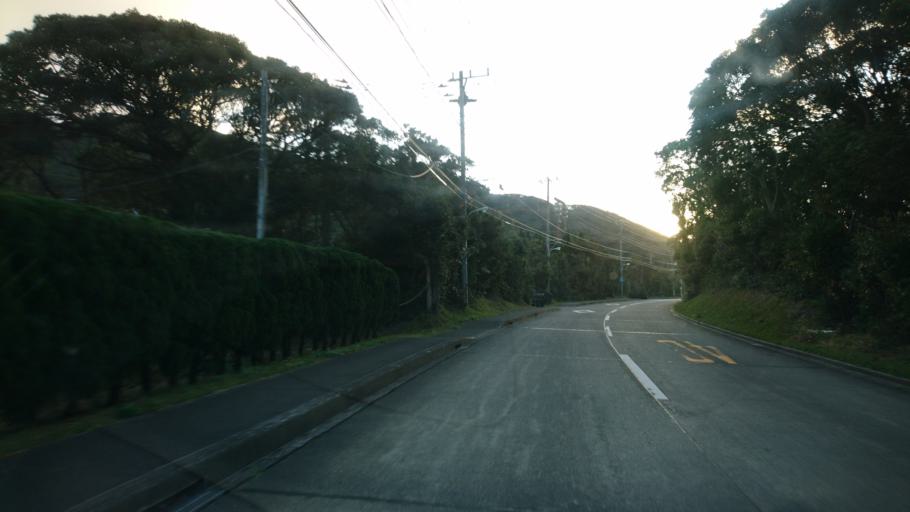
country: JP
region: Shizuoka
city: Shimoda
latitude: 34.3639
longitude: 139.2573
